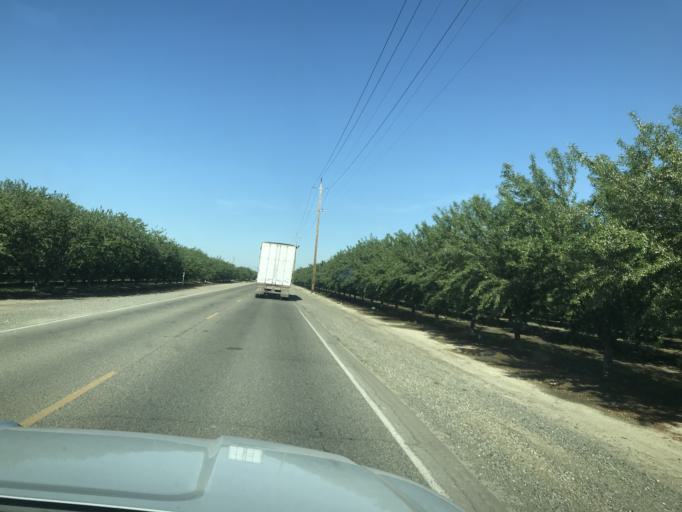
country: US
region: California
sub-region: Fresno County
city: Kerman
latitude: 36.6619
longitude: -120.1119
